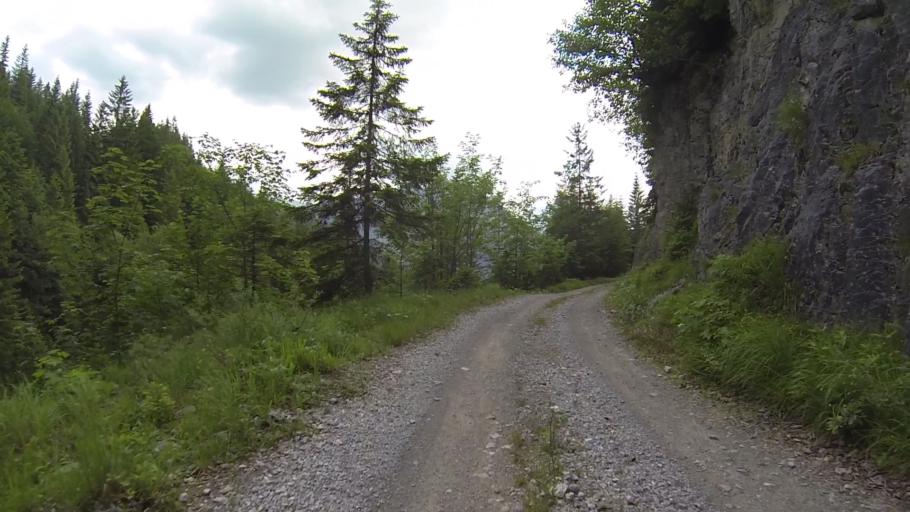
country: AT
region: Tyrol
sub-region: Politischer Bezirk Reutte
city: Breitenwang
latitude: 47.5050
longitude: 10.7587
